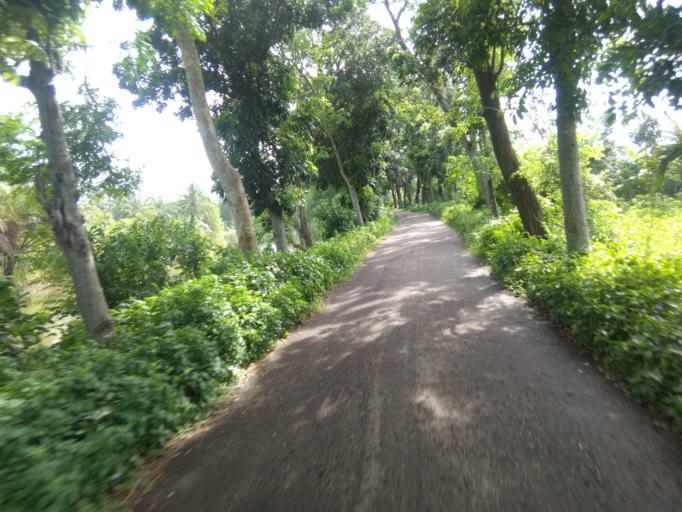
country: BD
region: Khulna
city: Kalia
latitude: 22.9505
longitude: 89.5474
